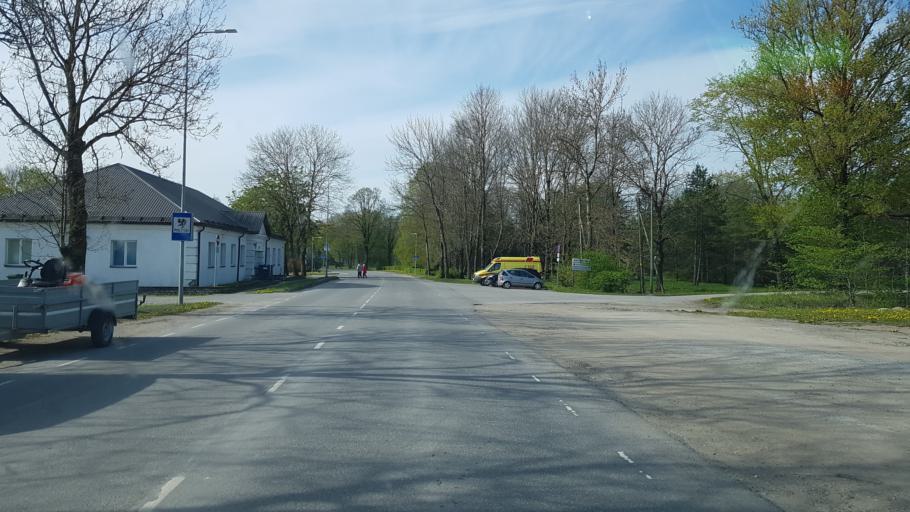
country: EE
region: Ida-Virumaa
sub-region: Kivioli linn
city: Kivioli
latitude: 59.3596
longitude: 26.9677
